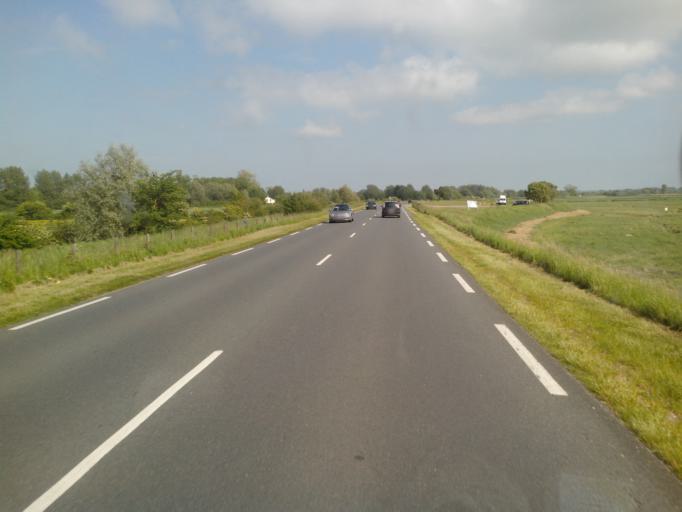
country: FR
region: Picardie
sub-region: Departement de la Somme
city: Le Crotoy
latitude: 50.2110
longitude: 1.6733
